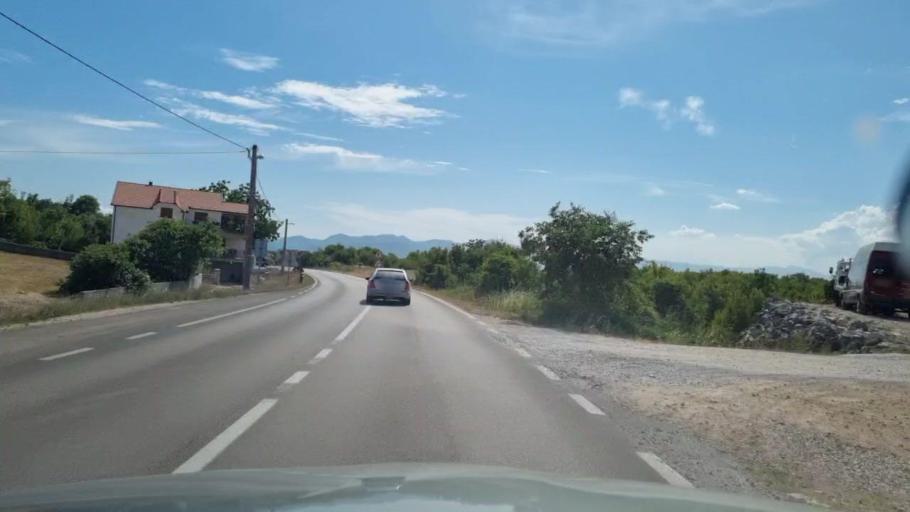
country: BA
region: Federation of Bosnia and Herzegovina
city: Kocerin
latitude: 43.3587
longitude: 17.4909
